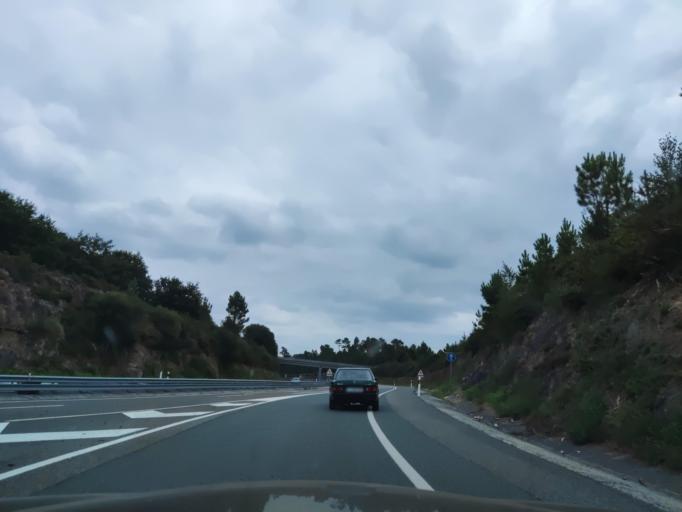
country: ES
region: Galicia
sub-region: Provincia da Coruna
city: Teo
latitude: 42.7879
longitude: -8.5453
